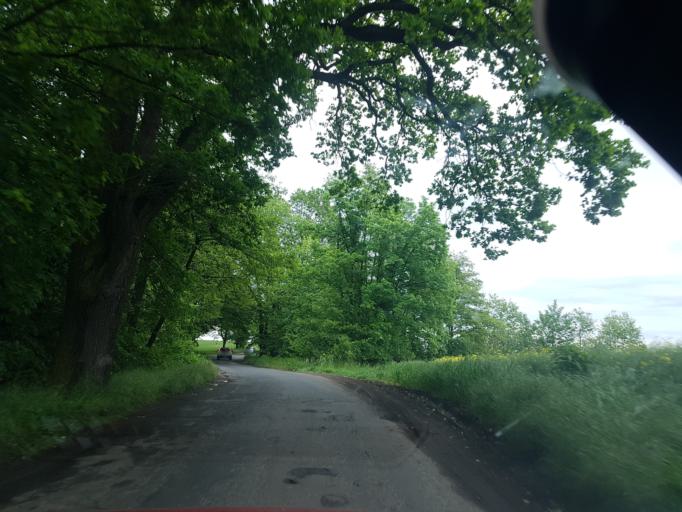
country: PL
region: Lower Silesian Voivodeship
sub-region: Powiat wroclawski
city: Katy Wroclawskie
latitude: 50.9814
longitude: 16.7661
